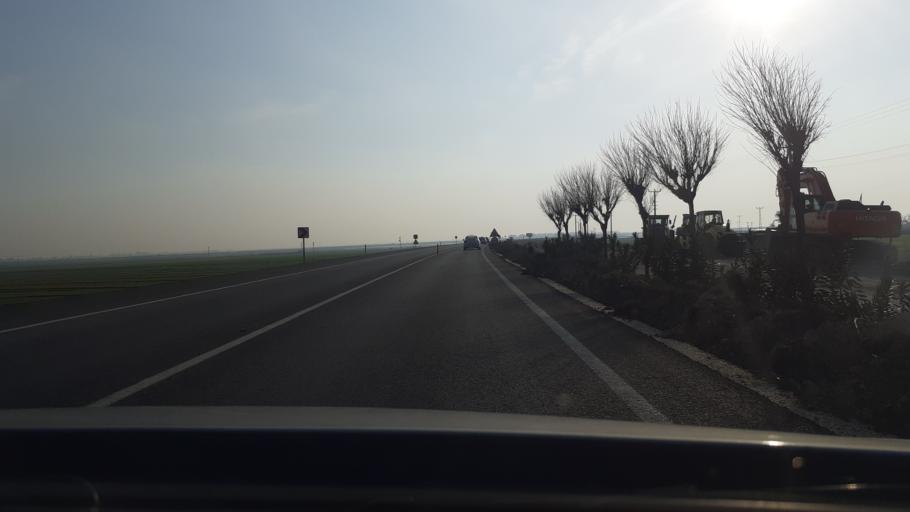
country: TR
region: Hatay
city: Serinyol
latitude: 36.3709
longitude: 36.2506
